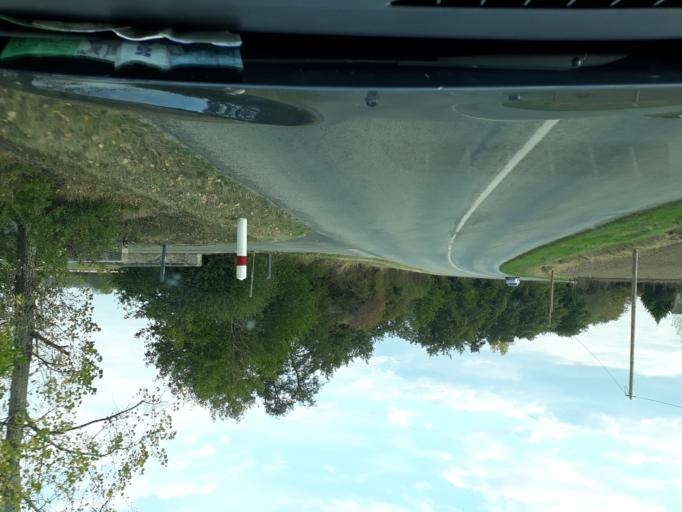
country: FR
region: Centre
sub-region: Departement du Loiret
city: Saint-Benoit-sur-Loire
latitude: 47.8350
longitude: 2.2735
